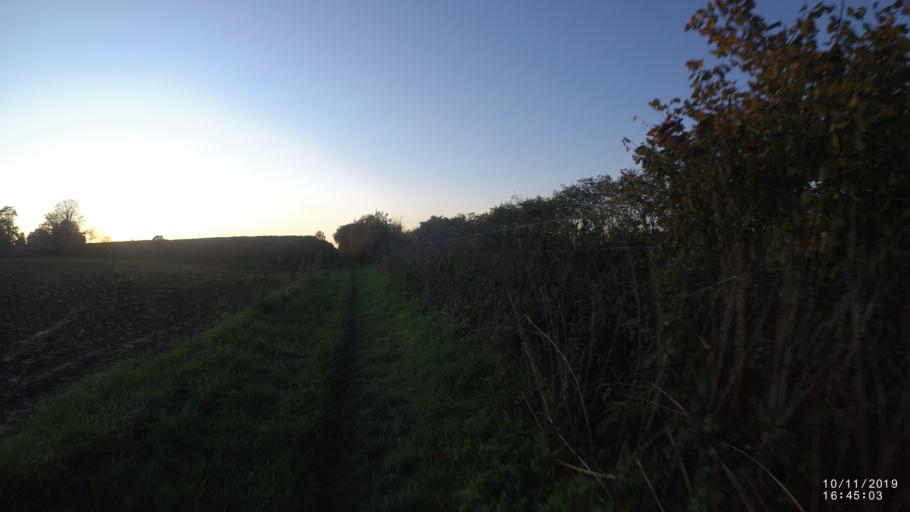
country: BE
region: Flanders
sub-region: Provincie Vlaams-Brabant
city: Bierbeek
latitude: 50.8559
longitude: 4.7533
